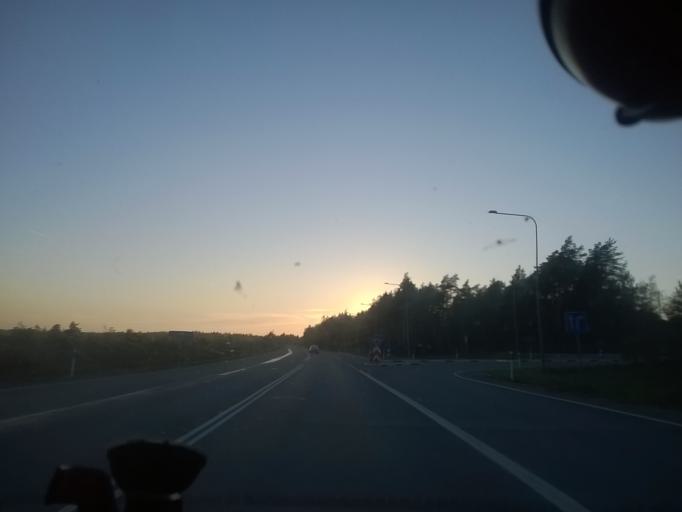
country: EE
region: Harju
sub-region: Nissi vald
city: Turba
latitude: 58.9972
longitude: 24.0755
